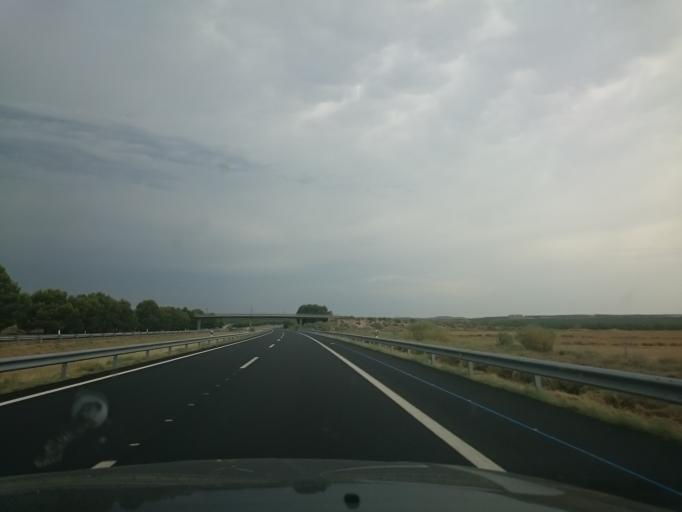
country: ES
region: Aragon
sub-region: Provincia de Zaragoza
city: Pina de Ebro
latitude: 41.5363
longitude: -0.5202
